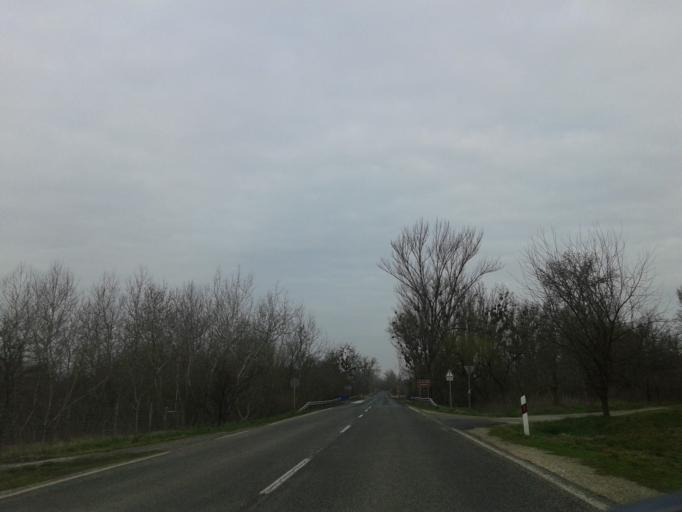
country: HU
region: Komarom-Esztergom
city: Dunaalmas
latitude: 47.6969
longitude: 18.3058
